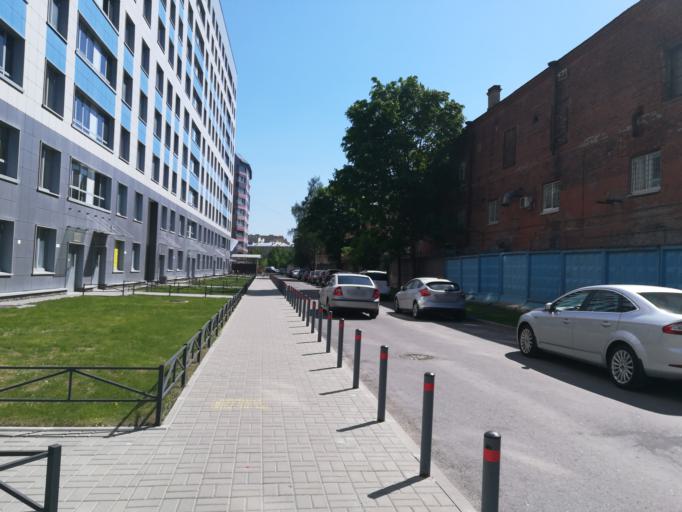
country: RU
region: St.-Petersburg
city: Vasyl'evsky Ostrov
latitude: 59.9502
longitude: 30.2610
